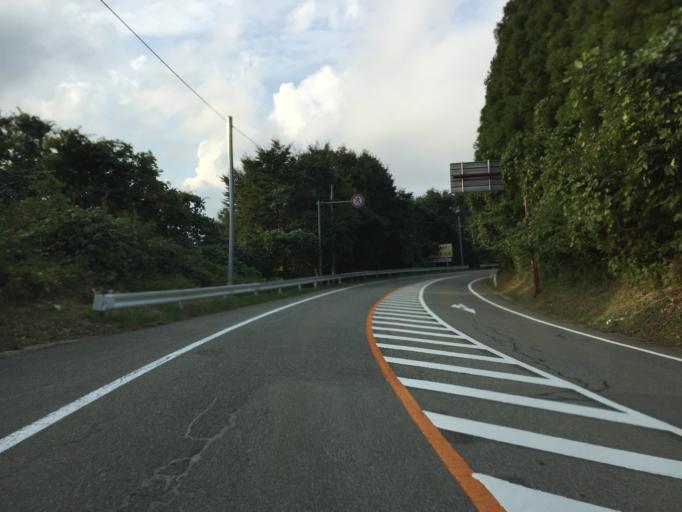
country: JP
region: Fukushima
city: Funehikimachi-funehiki
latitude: 37.5620
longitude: 140.7432
